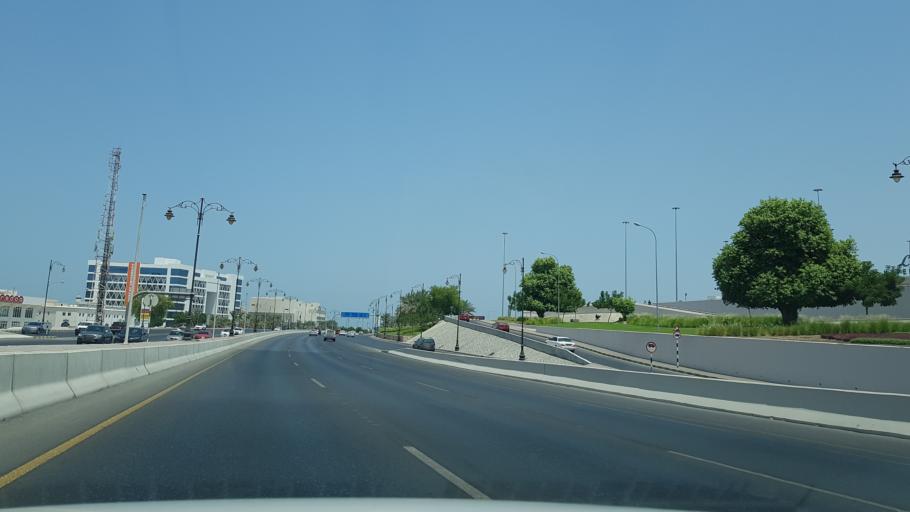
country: OM
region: Muhafazat Masqat
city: Bawshar
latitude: 23.5908
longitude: 58.4086
